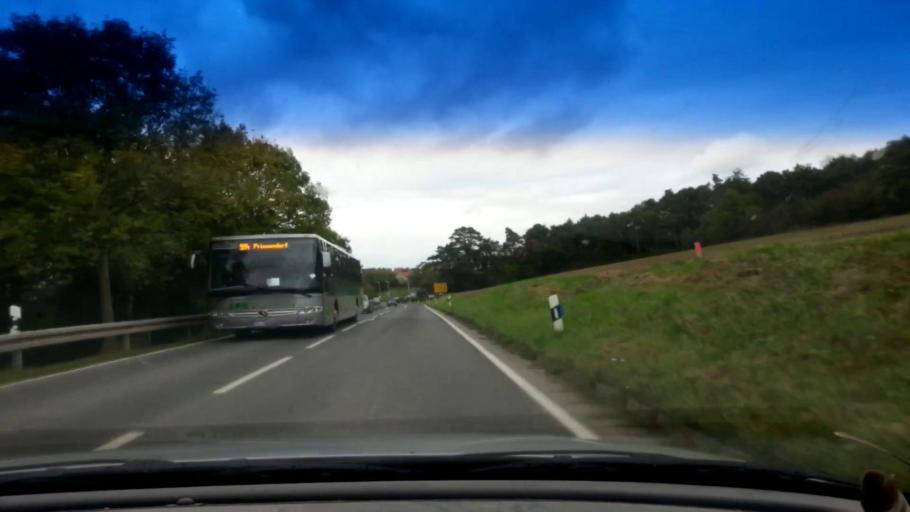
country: DE
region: Bavaria
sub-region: Upper Franconia
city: Priesendorf
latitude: 49.9003
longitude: 10.7168
